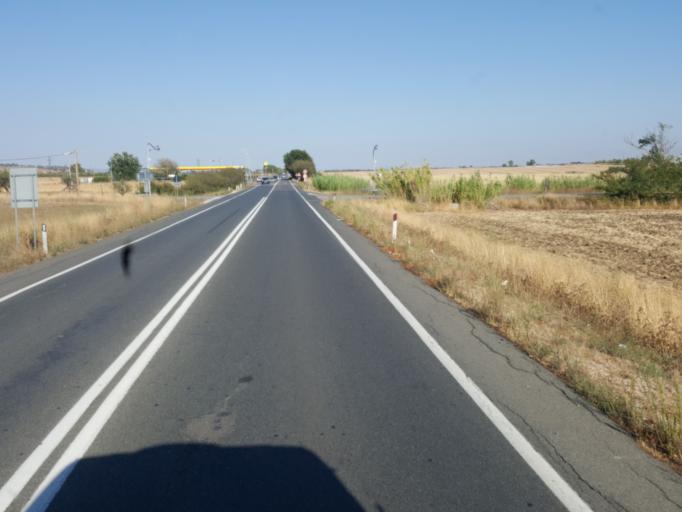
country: IT
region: Tuscany
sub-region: Provincia di Grosseto
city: Capalbio
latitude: 42.4146
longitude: 11.4222
